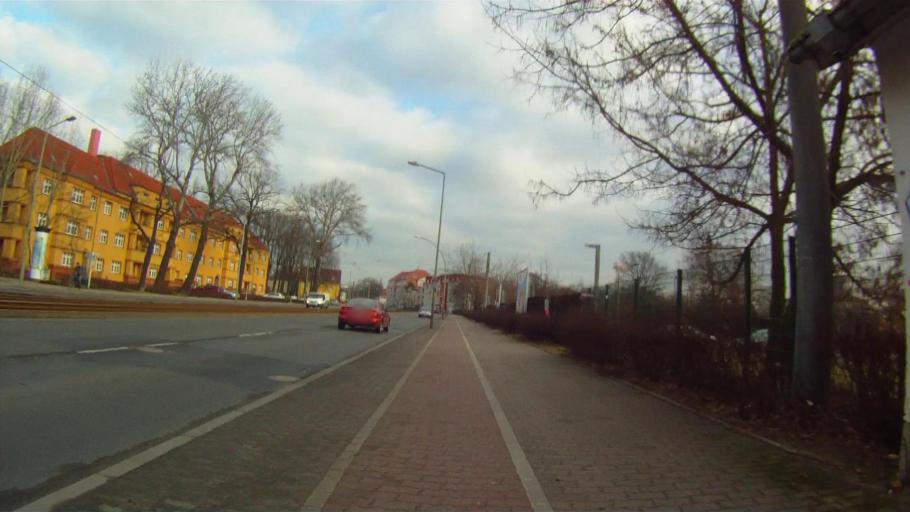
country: DE
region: Berlin
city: Karlshorst
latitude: 52.4764
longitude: 13.5230
